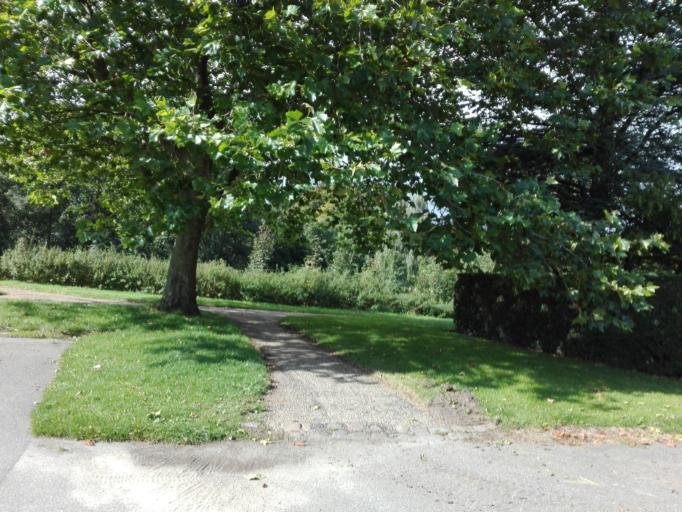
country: DK
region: Central Jutland
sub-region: Arhus Kommune
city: Beder
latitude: 56.0629
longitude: 10.2092
